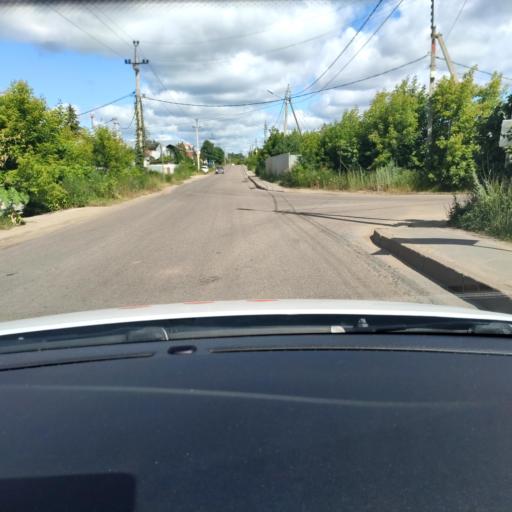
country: RU
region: Tatarstan
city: Vysokaya Gora
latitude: 55.8612
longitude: 49.2394
